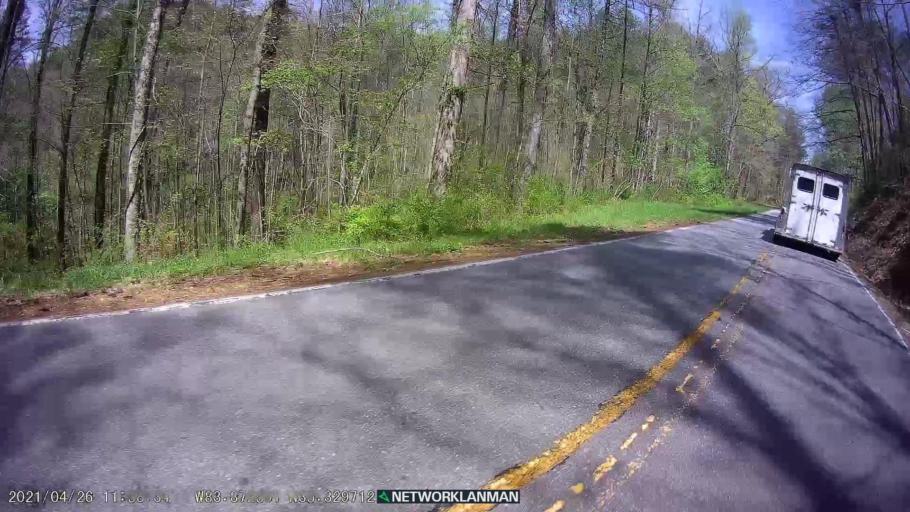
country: US
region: North Carolina
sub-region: Graham County
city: Robbinsville
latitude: 35.3297
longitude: -83.8724
